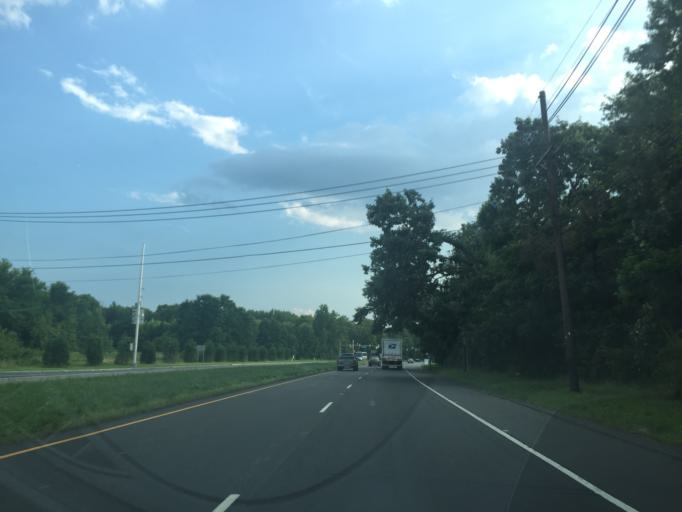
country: US
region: New Jersey
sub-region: Middlesex County
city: Cranbury
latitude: 40.3033
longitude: -74.5114
